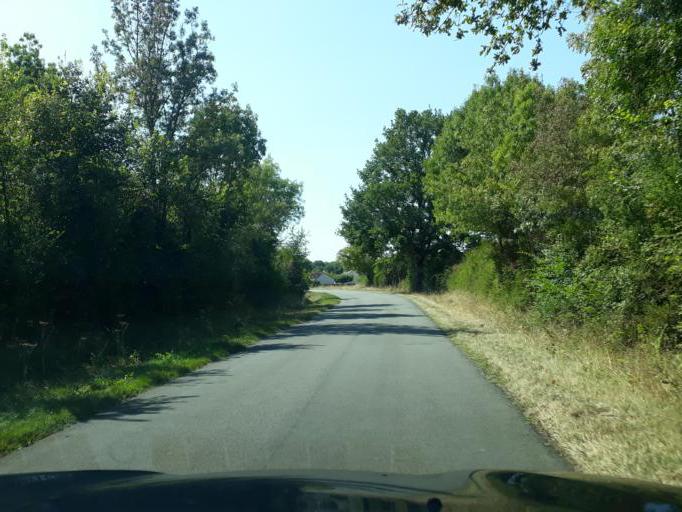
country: FR
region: Centre
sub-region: Departement du Loir-et-Cher
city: Gievres
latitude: 47.2576
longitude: 1.6807
